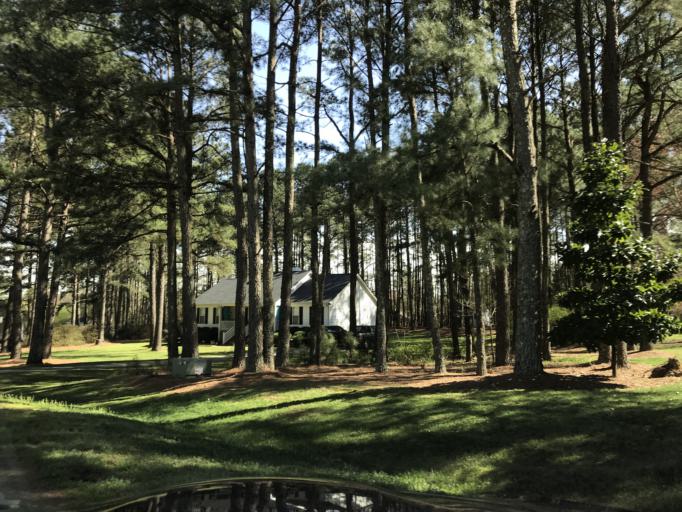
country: US
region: North Carolina
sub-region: Wake County
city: Wendell
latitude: 35.7728
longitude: -78.4013
